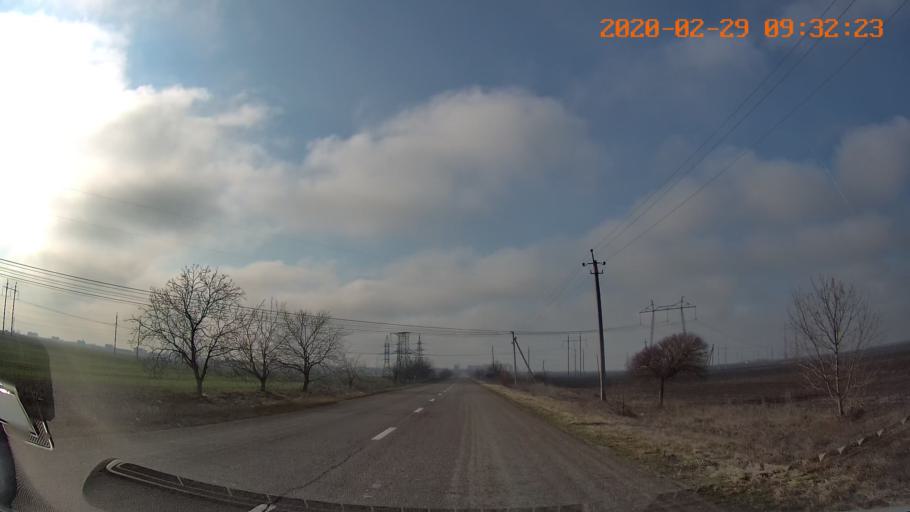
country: MD
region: Telenesti
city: Dnestrovsc
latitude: 46.6402
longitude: 29.9063
